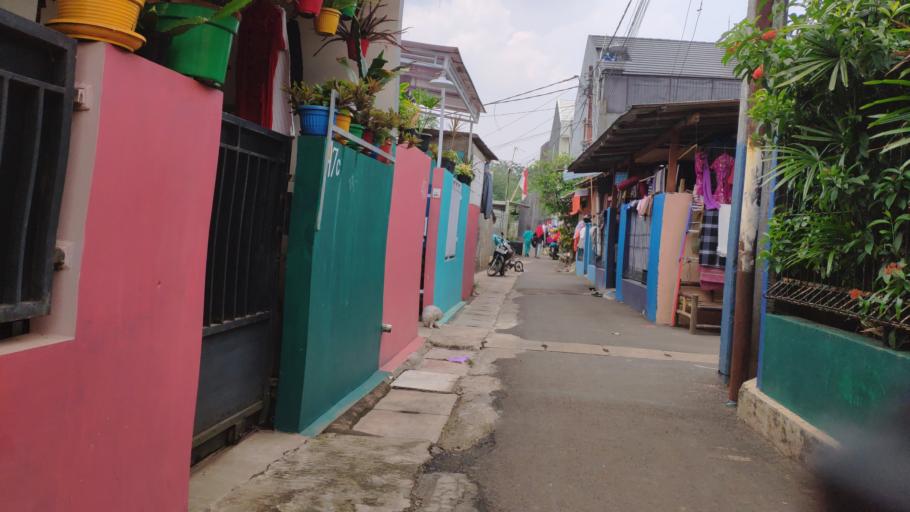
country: ID
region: West Java
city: Depok
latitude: -6.3153
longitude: 106.8299
